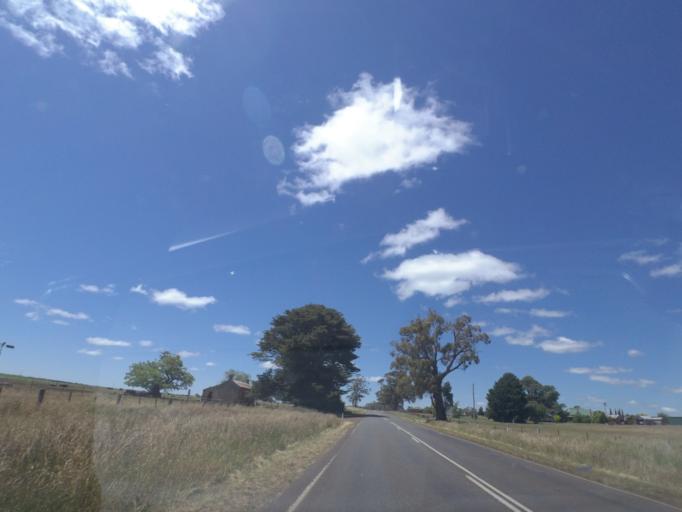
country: AU
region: Victoria
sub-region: Mount Alexander
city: Castlemaine
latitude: -37.3098
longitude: 144.2298
